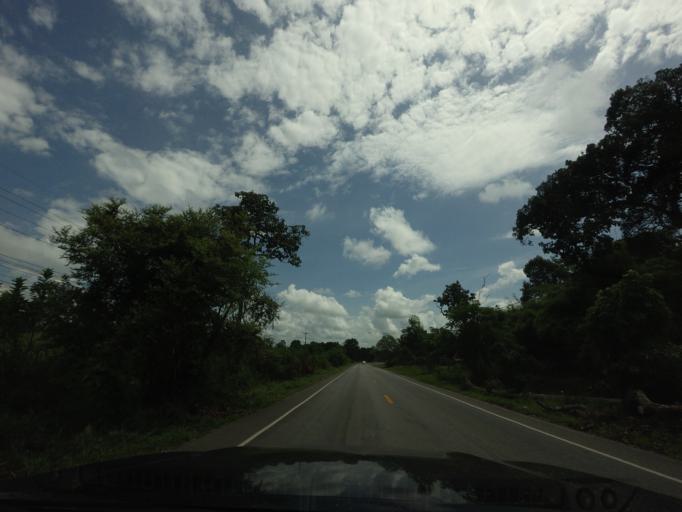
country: TH
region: Nong Khai
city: Pho Tak
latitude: 17.8062
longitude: 102.3373
